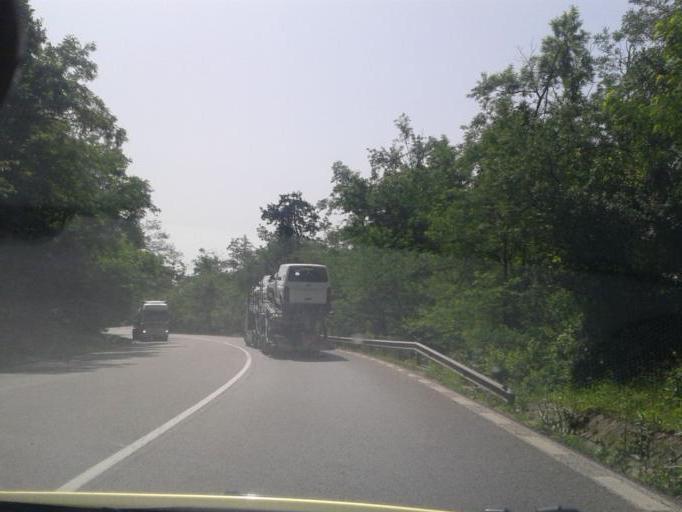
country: RO
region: Arges
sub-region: Comuna Cotmeana
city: Cotmeana
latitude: 44.9747
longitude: 24.6640
